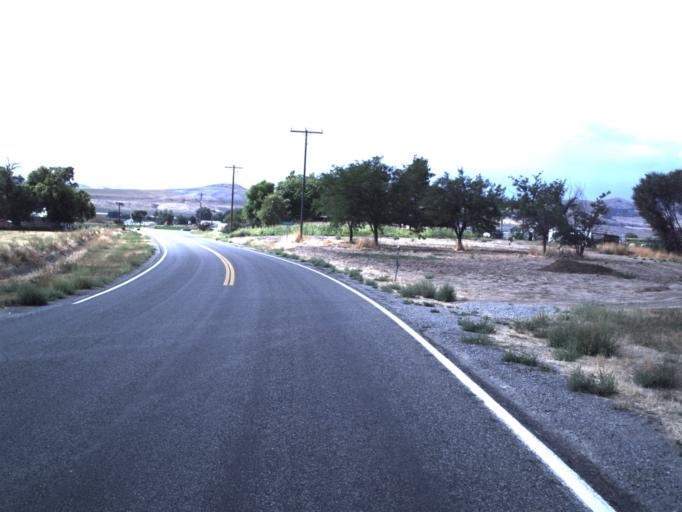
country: US
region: Utah
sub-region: Cache County
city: Lewiston
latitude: 41.9164
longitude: -111.9329
